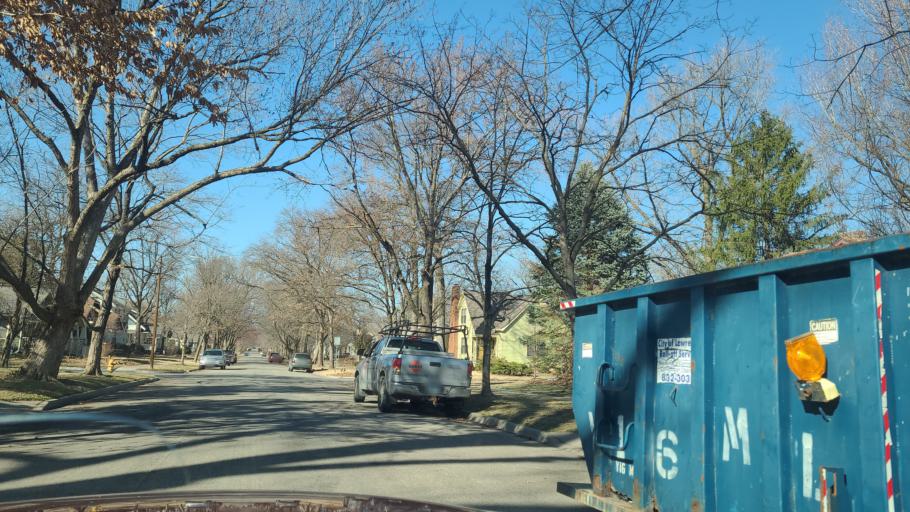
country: US
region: Kansas
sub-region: Douglas County
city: Lawrence
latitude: 38.9442
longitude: -95.2347
